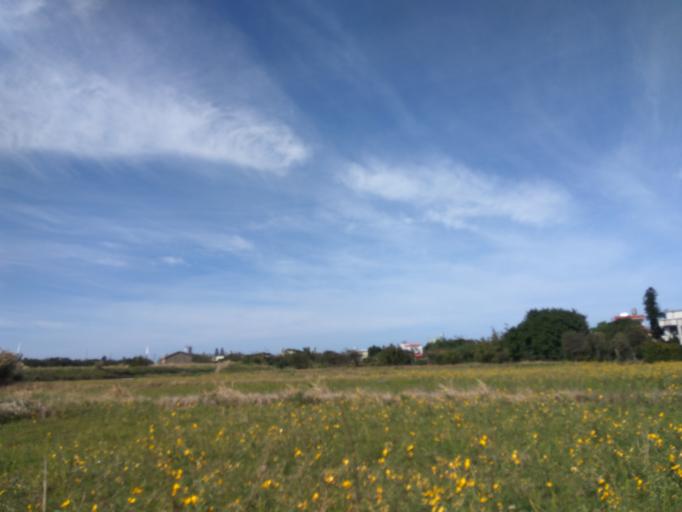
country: TW
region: Taiwan
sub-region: Hsinchu
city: Zhubei
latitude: 25.0212
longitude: 121.0635
